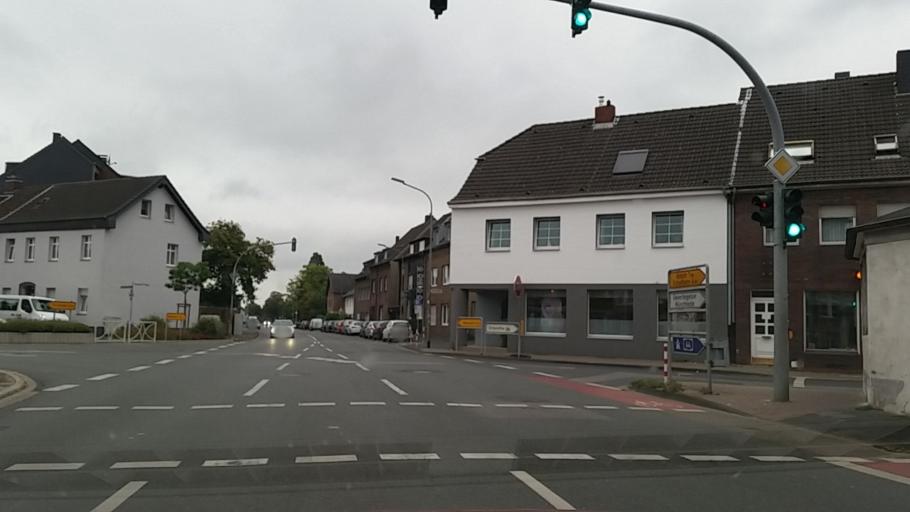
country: DE
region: North Rhine-Westphalia
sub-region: Regierungsbezirk Dusseldorf
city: Willich
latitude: 51.2665
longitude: 6.5532
